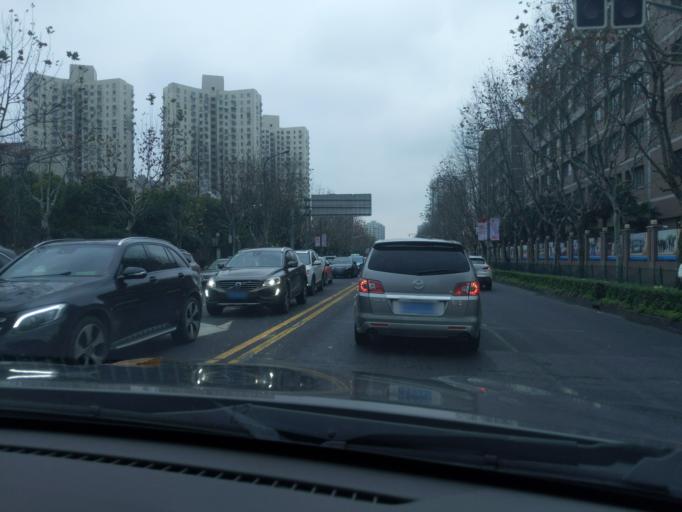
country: CN
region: Shanghai Shi
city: Huamu
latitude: 31.1874
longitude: 121.5054
